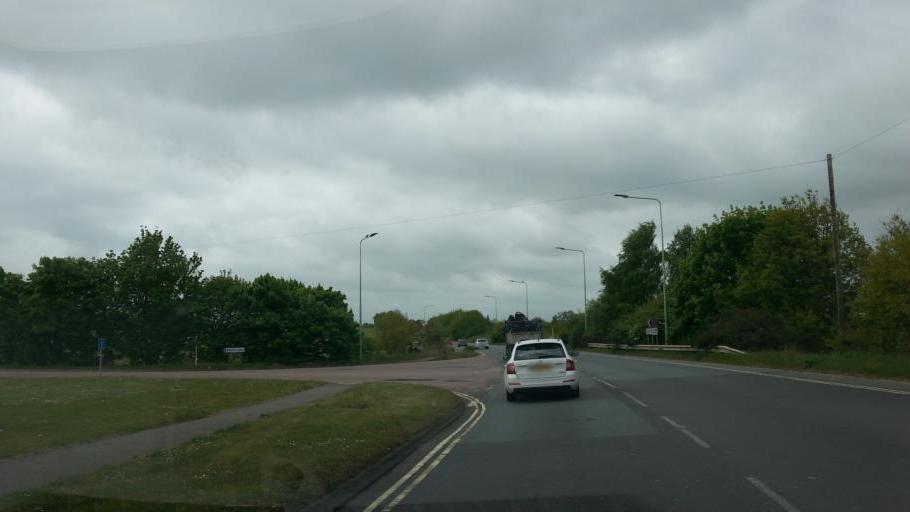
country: GB
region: England
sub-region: Suffolk
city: Bramford
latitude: 52.0471
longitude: 1.1063
